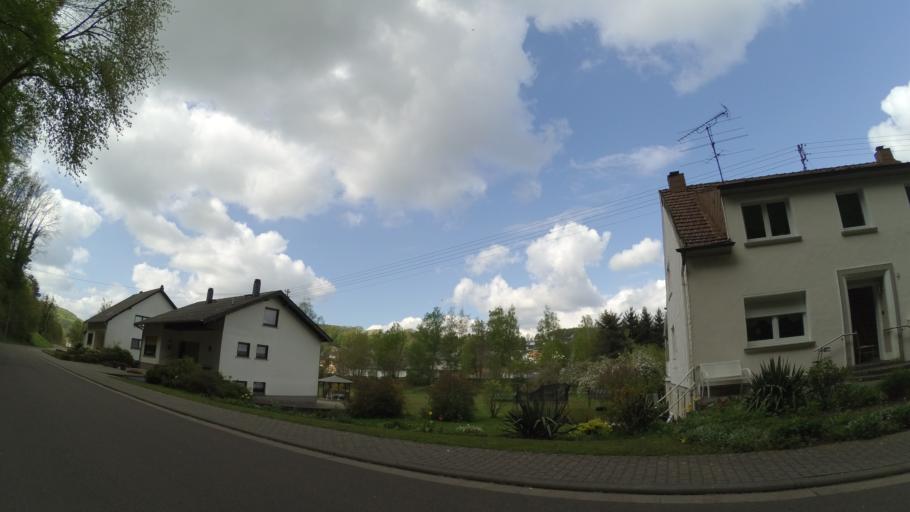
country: DE
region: Saarland
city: Wadern
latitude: 49.4938
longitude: 6.8700
